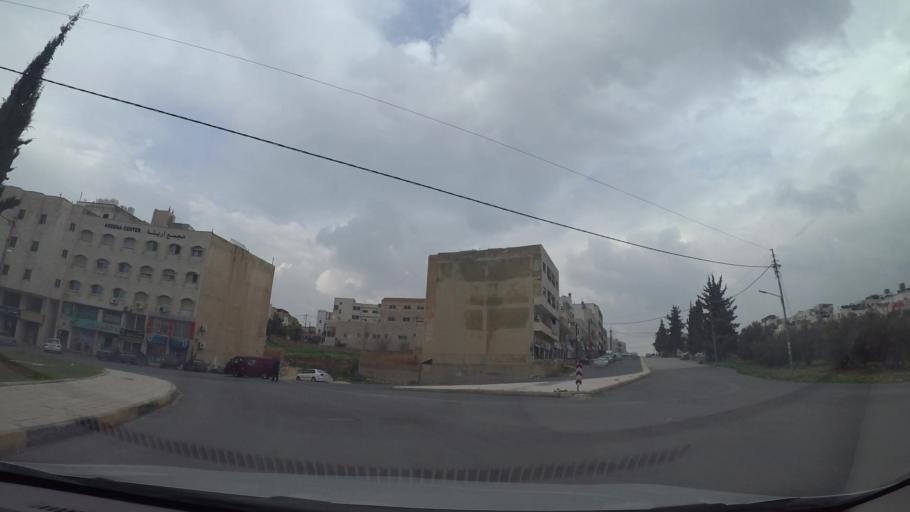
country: JO
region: Amman
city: Umm as Summaq
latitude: 31.8859
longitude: 35.8562
